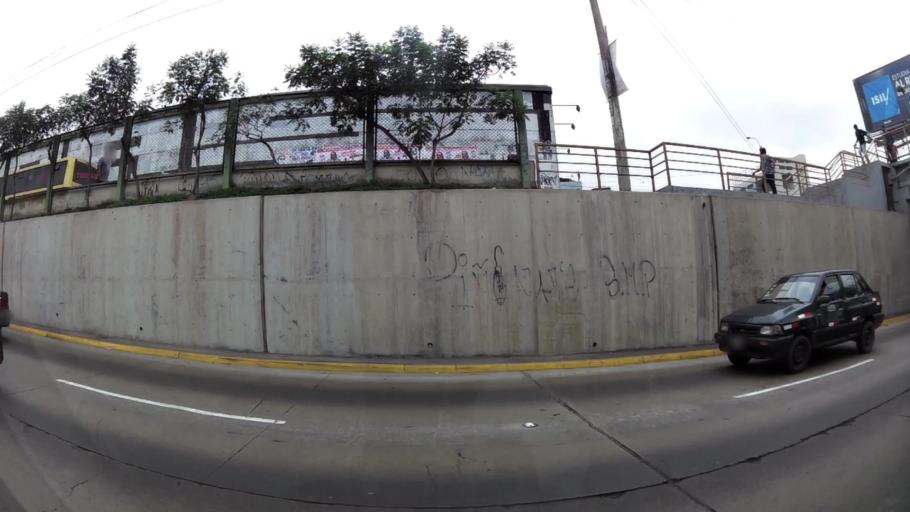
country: PE
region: Lima
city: Lima
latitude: -12.0691
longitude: -77.0322
